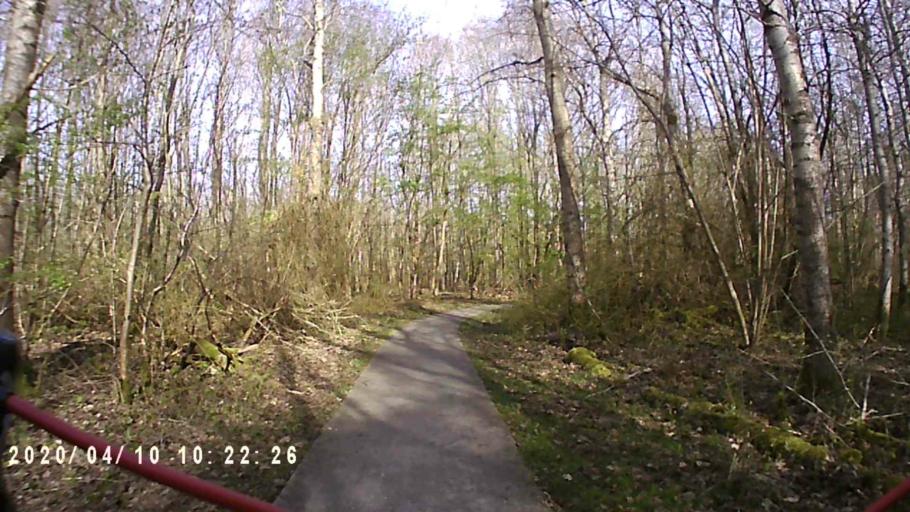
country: NL
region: Friesland
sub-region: Gemeente Dongeradeel
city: Anjum
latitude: 53.3837
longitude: 6.2149
